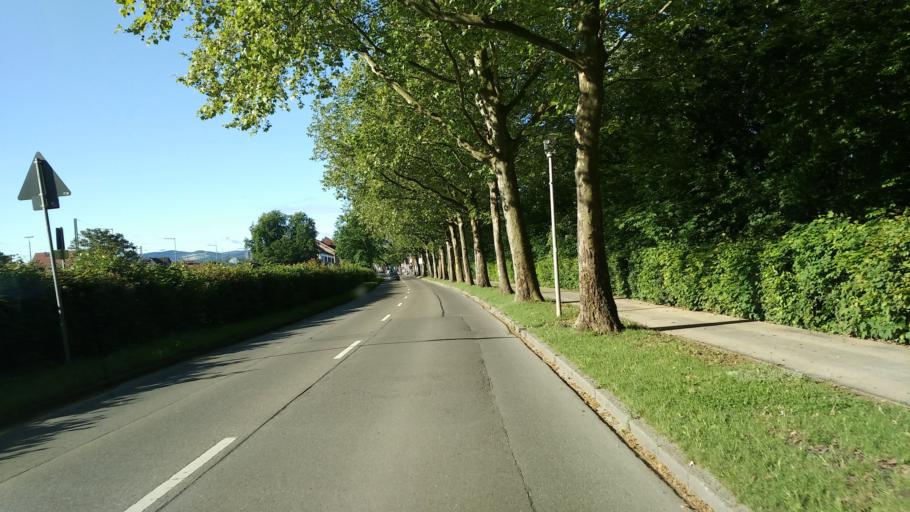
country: DE
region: Baden-Wuerttemberg
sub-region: Regierungsbezirk Stuttgart
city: Nurtingen
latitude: 48.6302
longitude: 9.3428
